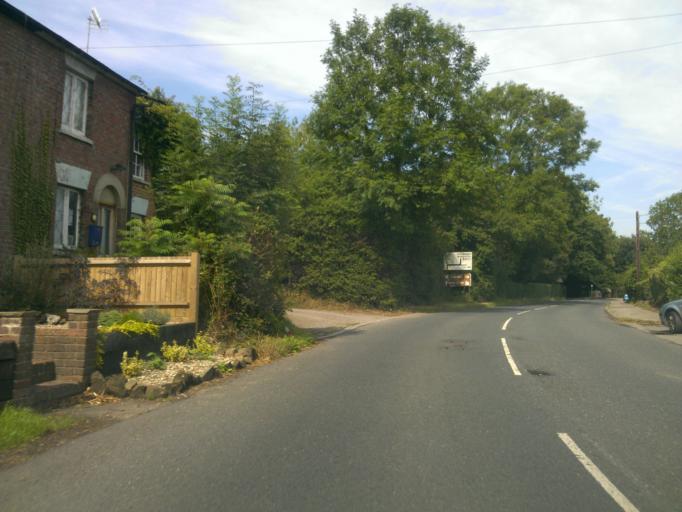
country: GB
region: England
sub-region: Kent
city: Edenbridge
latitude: 51.2000
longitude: 0.1323
